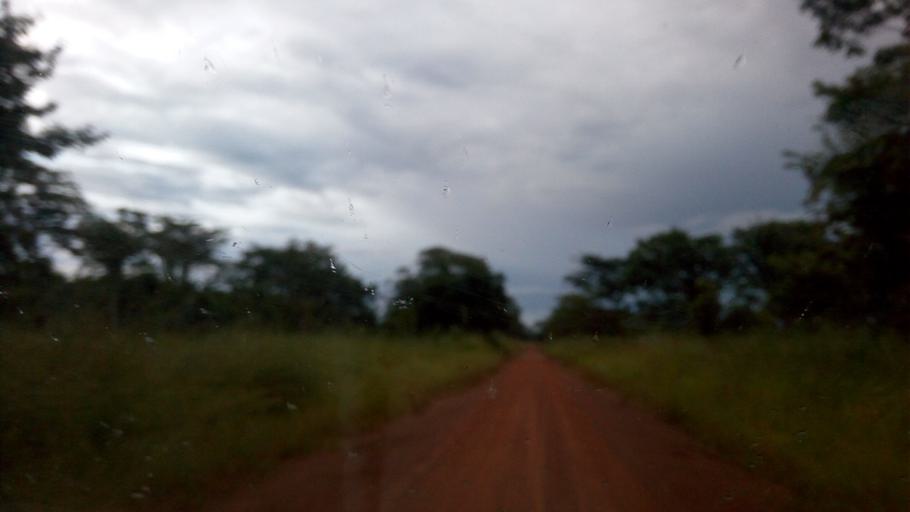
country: ZM
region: Luapula
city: Mwense
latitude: -9.9013
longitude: 28.0980
